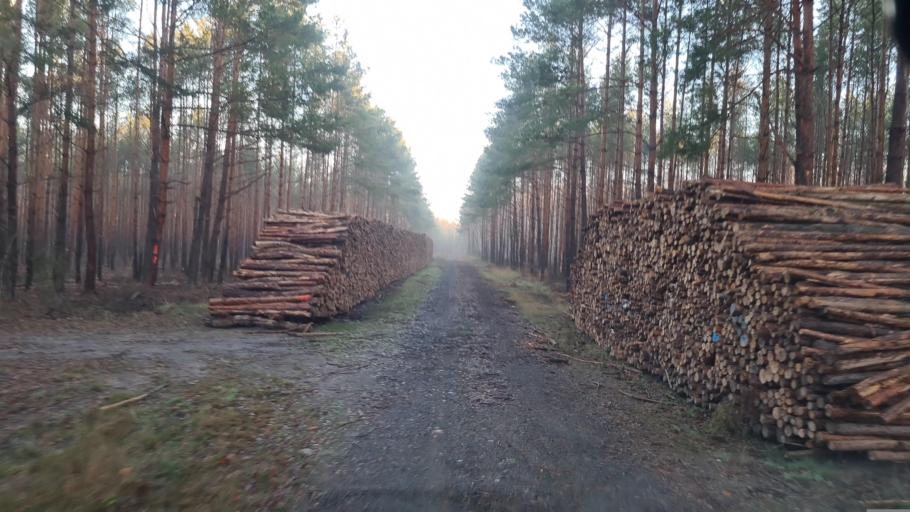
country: DE
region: Brandenburg
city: Lauchhammer
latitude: 51.5364
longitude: 13.7586
